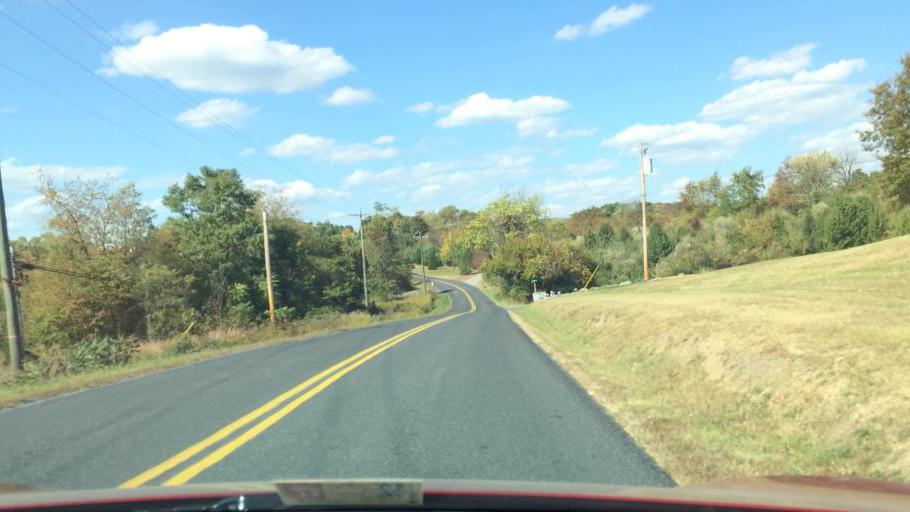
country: US
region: Virginia
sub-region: Frederick County
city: Shawnee Land
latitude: 39.3264
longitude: -78.3180
